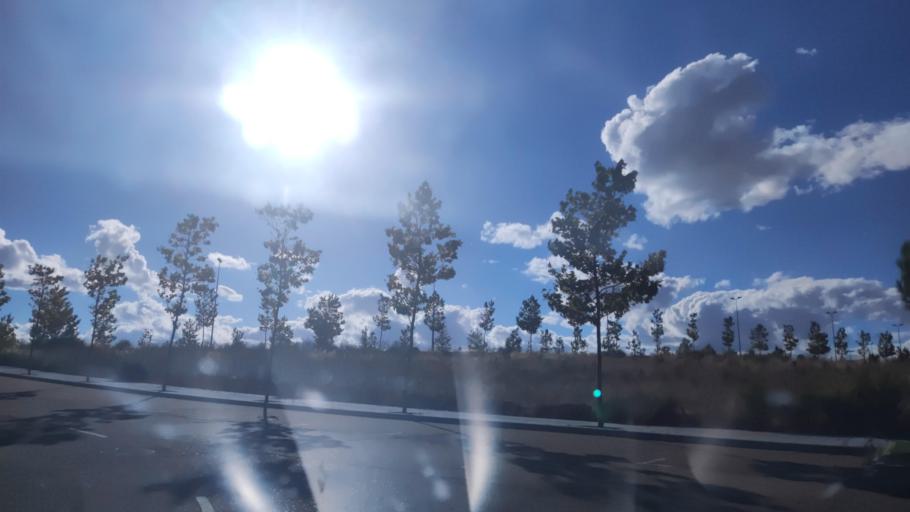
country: ES
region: Castille and Leon
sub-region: Provincia de Salamanca
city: Salamanca
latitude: 40.9716
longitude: -5.6864
